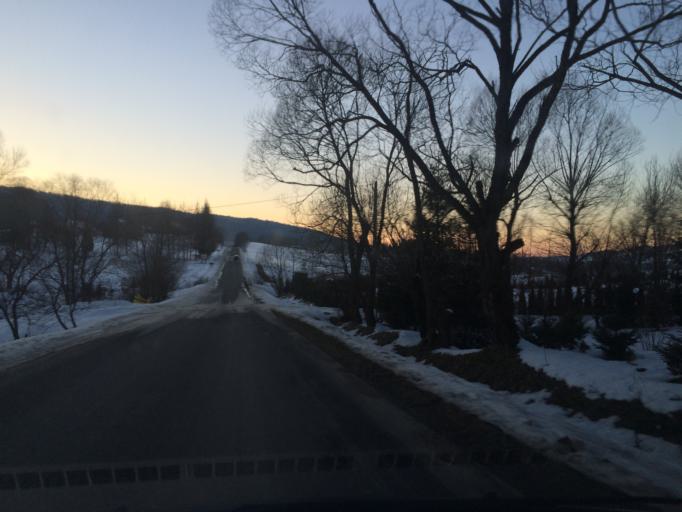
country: PL
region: Subcarpathian Voivodeship
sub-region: Powiat bieszczadzki
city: Ustrzyki Dolne
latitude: 49.4000
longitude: 22.6069
